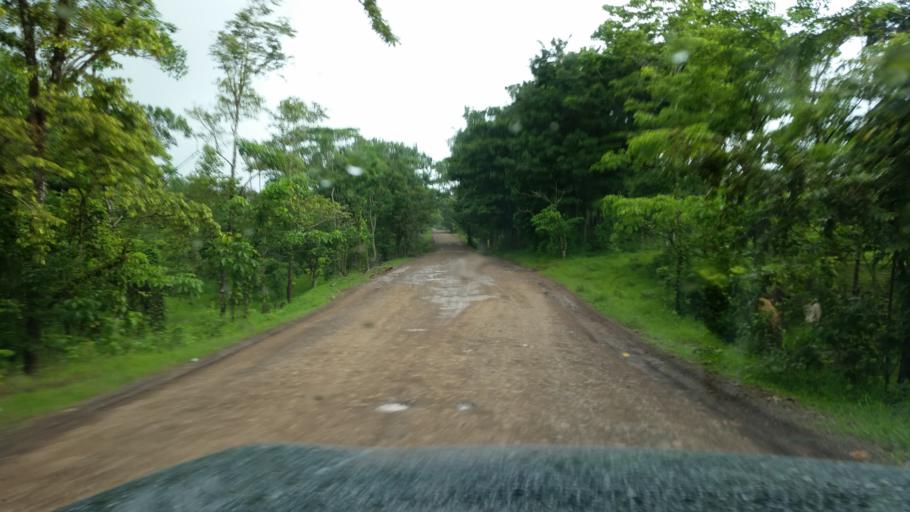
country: NI
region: Atlantico Norte (RAAN)
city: Siuna
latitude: 13.4111
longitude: -84.8538
